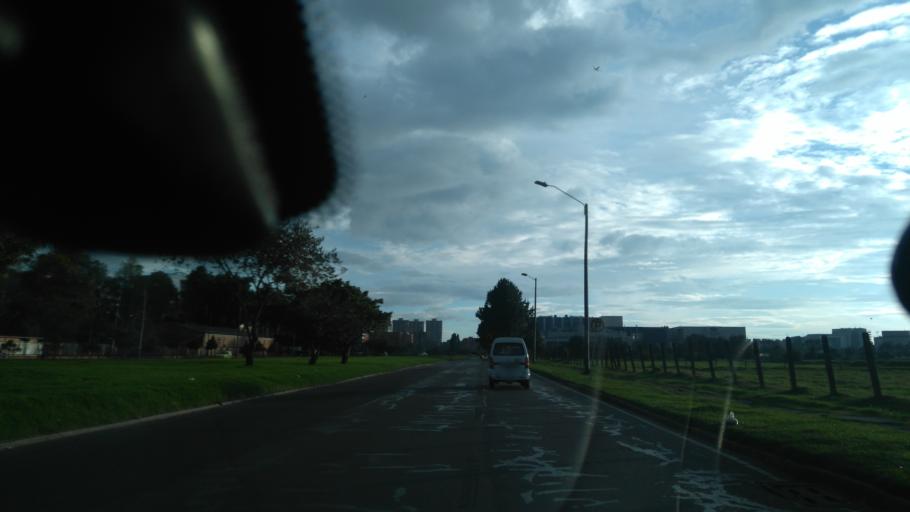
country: CO
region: Bogota D.C.
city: Bogota
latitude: 4.6500
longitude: -74.0962
